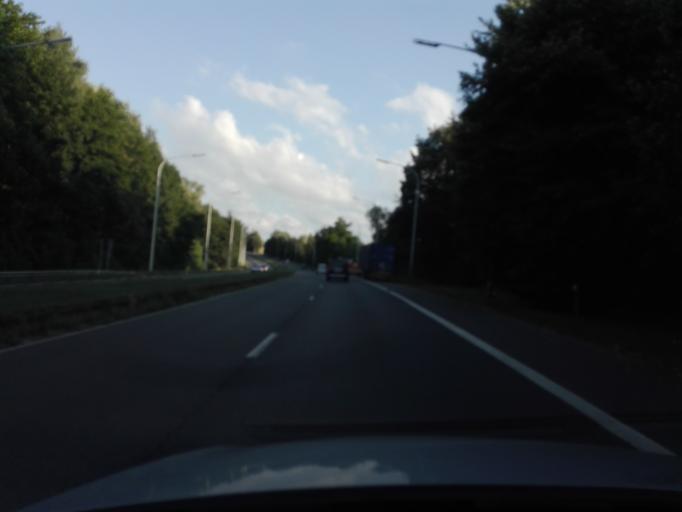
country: BE
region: Wallonia
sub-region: Province du Brabant Wallon
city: Louvain-la-Neuve
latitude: 50.6860
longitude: 4.6158
